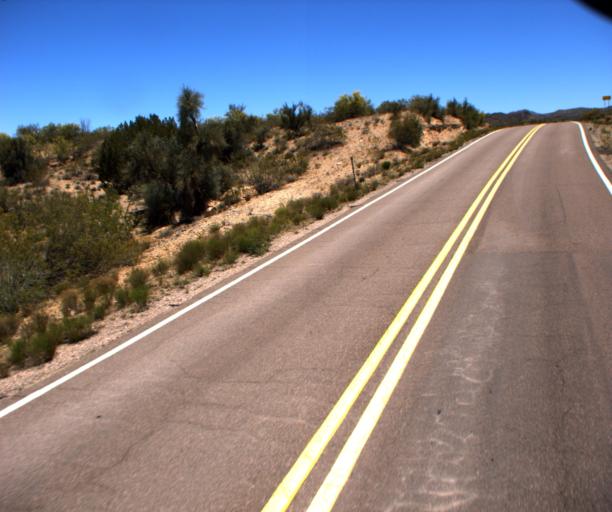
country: US
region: Arizona
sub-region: Yavapai County
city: Bagdad
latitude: 34.4700
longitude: -113.2179
